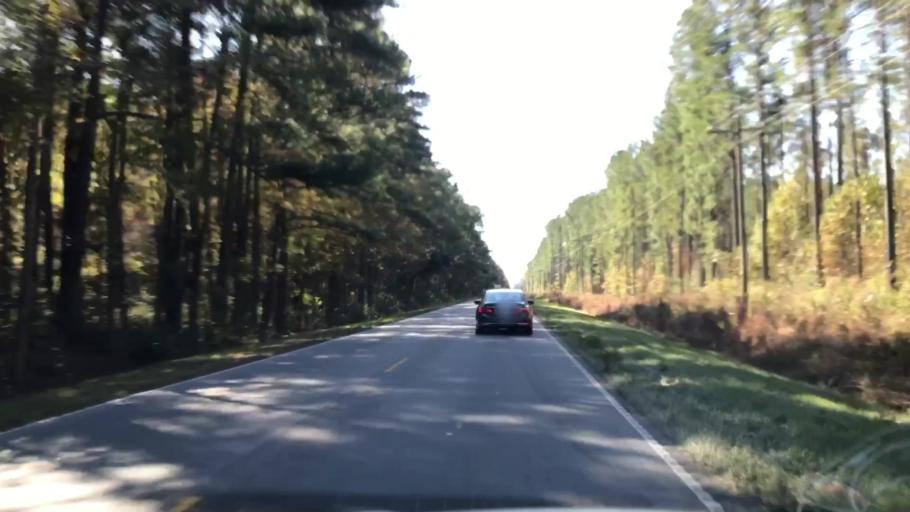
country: US
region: South Carolina
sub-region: Jasper County
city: Ridgeland
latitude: 32.3700
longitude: -80.9157
